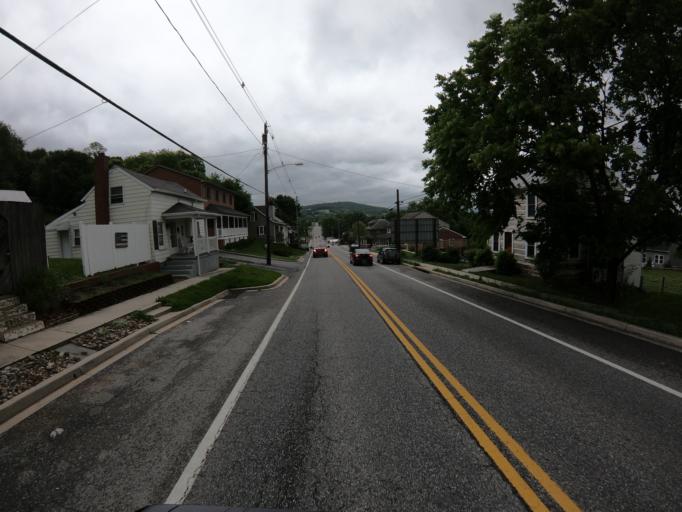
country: US
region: Maryland
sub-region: Washington County
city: Boonsboro
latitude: 39.5019
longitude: -77.6497
